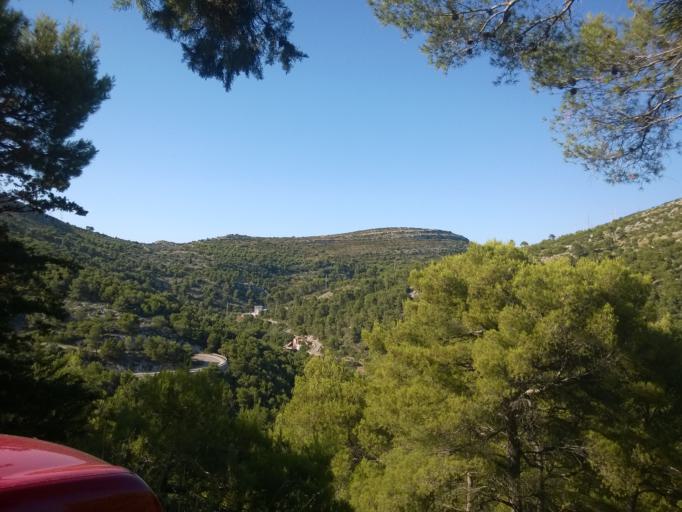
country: HR
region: Splitsko-Dalmatinska
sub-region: Grad Hvar
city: Hvar
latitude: 43.1751
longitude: 16.4416
